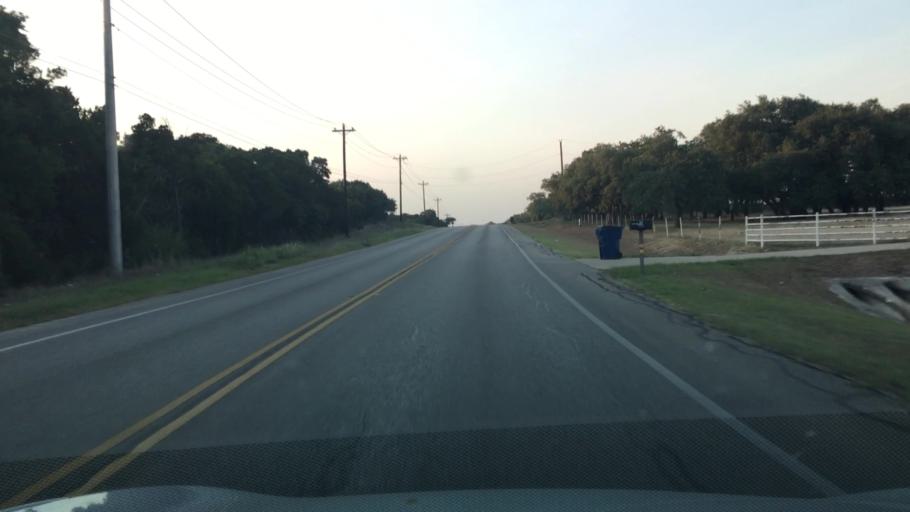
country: US
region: Texas
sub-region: Hays County
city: Dripping Springs
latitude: 30.1580
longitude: -98.0090
